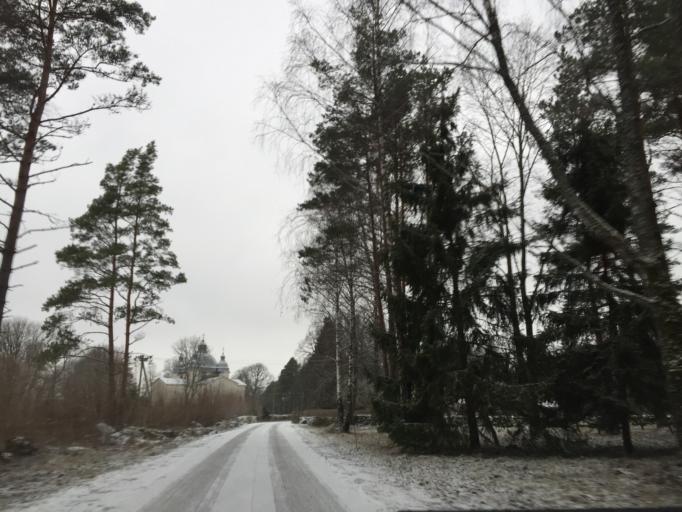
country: EE
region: Saare
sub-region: Orissaare vald
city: Orissaare
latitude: 58.6184
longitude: 23.1873
